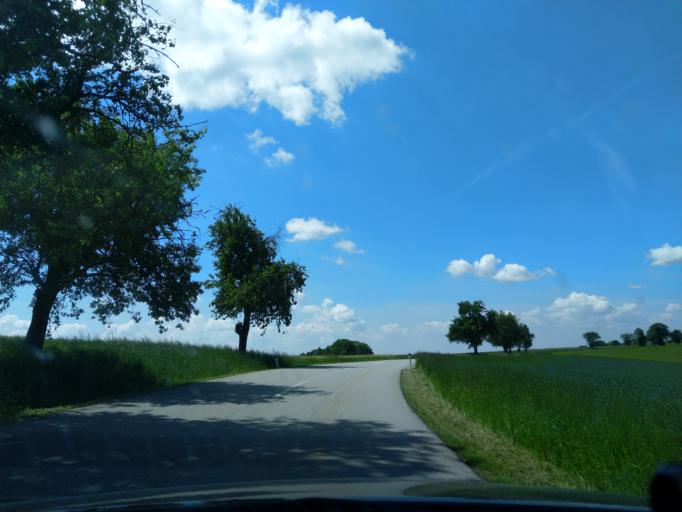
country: AT
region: Upper Austria
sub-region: Politischer Bezirk Ried im Innkreis
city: Ried im Innkreis
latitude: 48.1990
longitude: 13.5686
